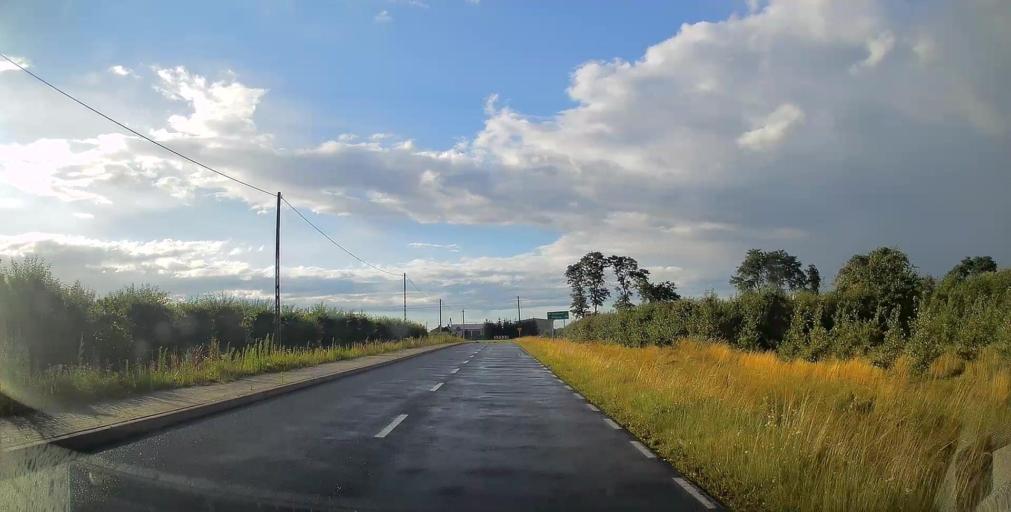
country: PL
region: Masovian Voivodeship
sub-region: Powiat grojecki
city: Goszczyn
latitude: 51.7631
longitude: 20.8994
